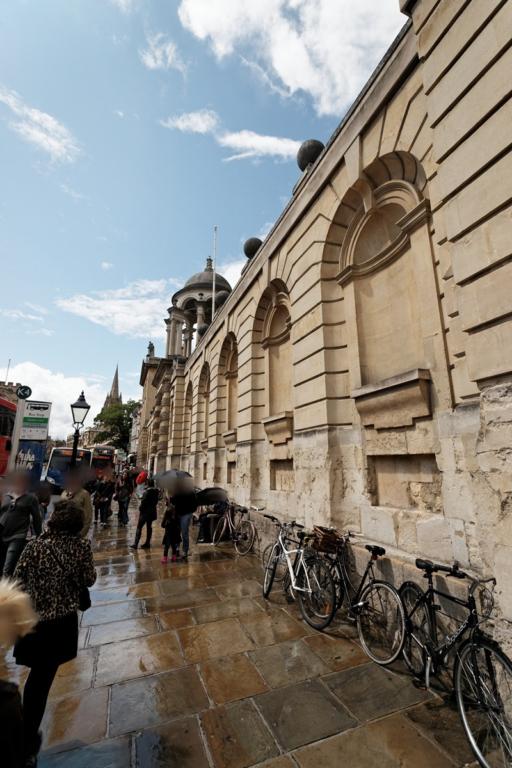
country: GB
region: England
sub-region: Oxfordshire
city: Oxford
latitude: 51.7528
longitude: -1.2508
